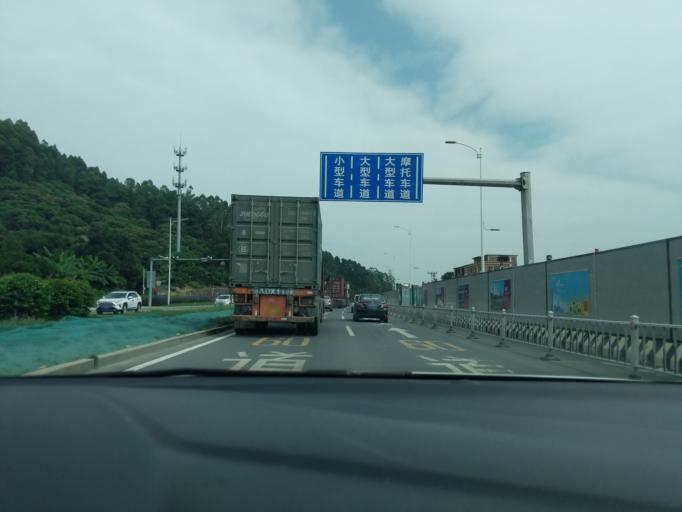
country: CN
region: Guangdong
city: Nansha
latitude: 22.7553
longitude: 113.5712
